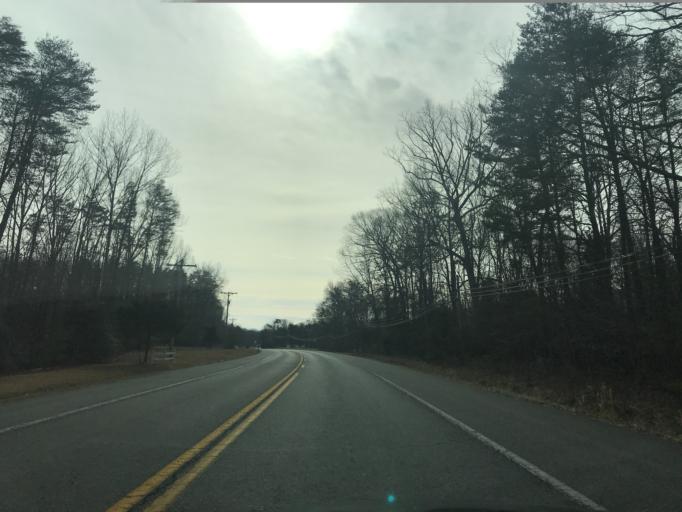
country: US
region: Virginia
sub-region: Prince William County
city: Quantico Station
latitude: 38.4670
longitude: -77.2210
